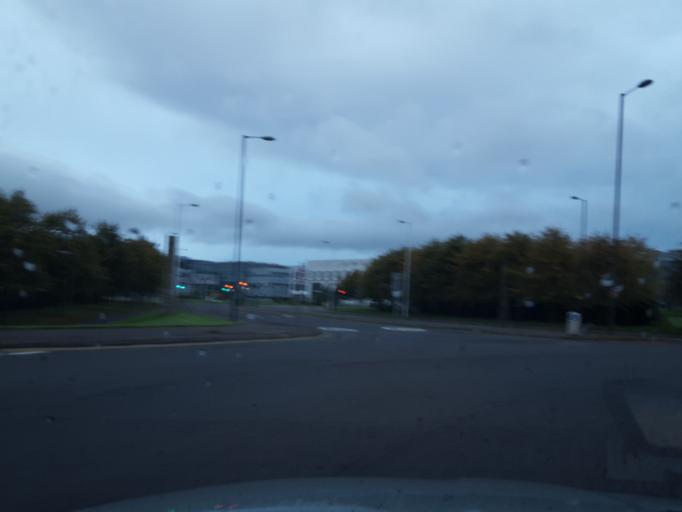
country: GB
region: Scotland
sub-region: Edinburgh
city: Currie
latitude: 55.9363
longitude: -3.3153
